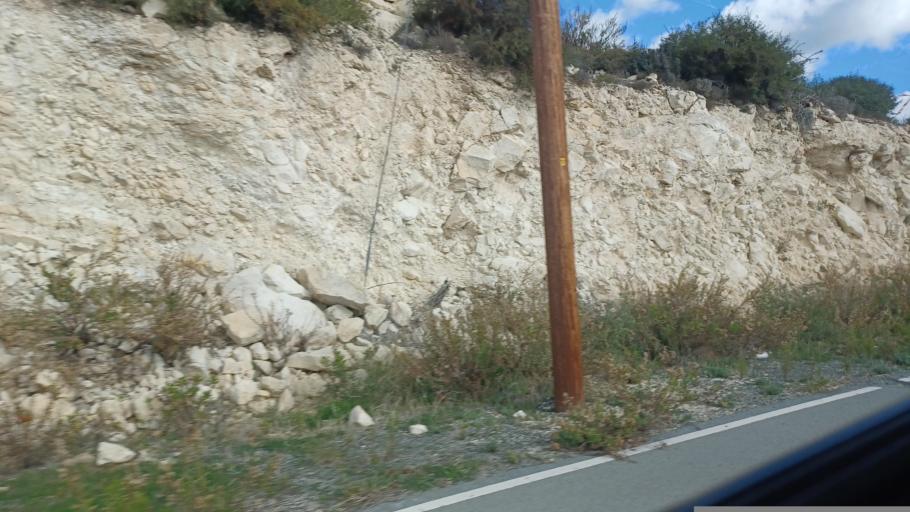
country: CY
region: Limassol
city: Pano Polemidia
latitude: 34.7933
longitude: 32.9865
